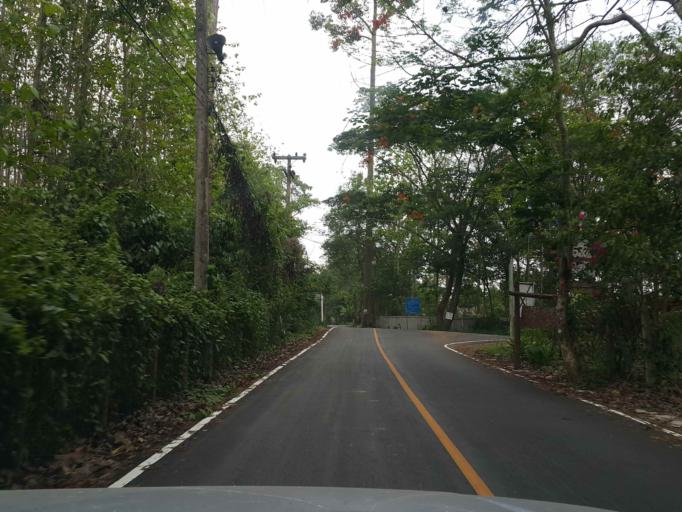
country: TH
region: Chiang Mai
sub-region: Amphoe Chiang Dao
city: Chiang Dao
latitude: 19.4023
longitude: 98.9282
